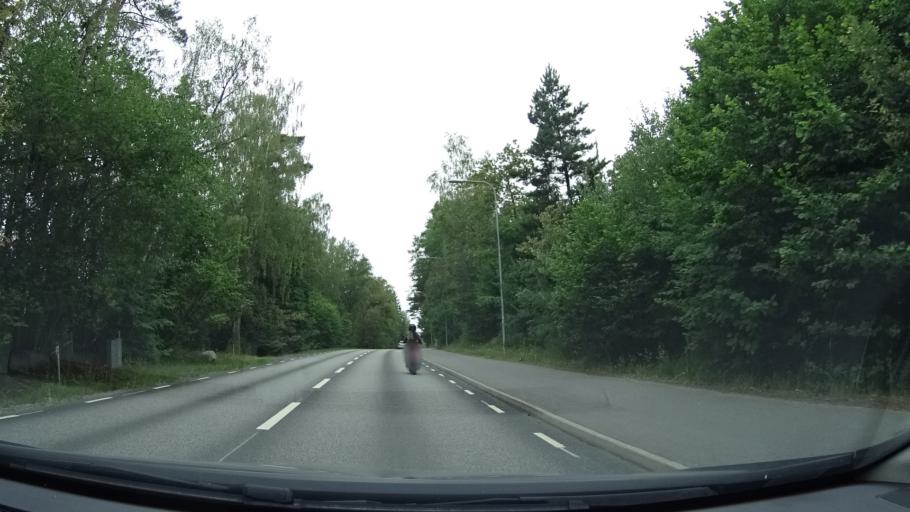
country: SE
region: Stockholm
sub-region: Varmdo Kommun
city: Hemmesta
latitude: 59.3332
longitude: 18.4926
